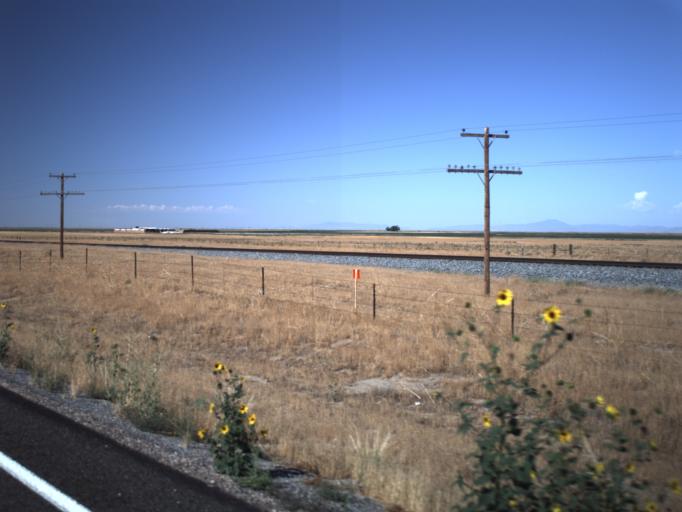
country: US
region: Utah
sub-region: Millard County
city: Delta
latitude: 39.5631
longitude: -112.3483
